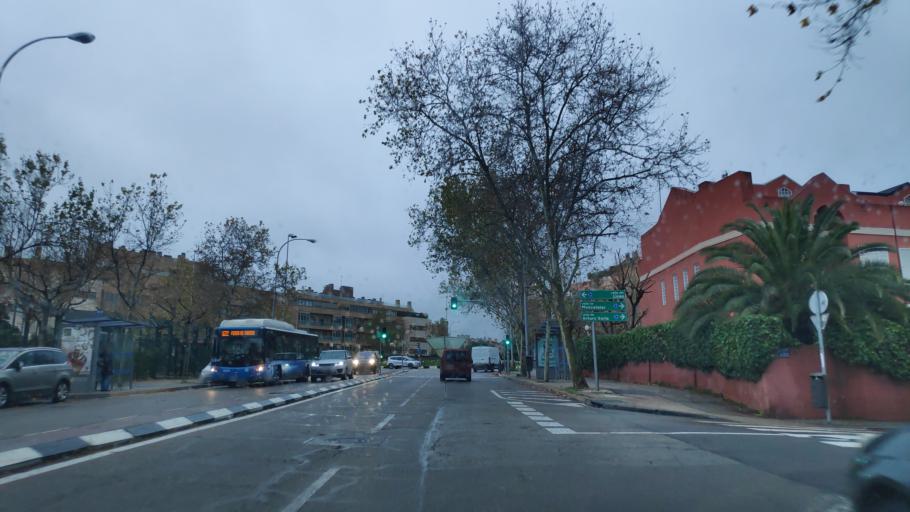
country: ES
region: Madrid
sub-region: Provincia de Madrid
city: Ciudad Lineal
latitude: 40.4581
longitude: -3.6437
